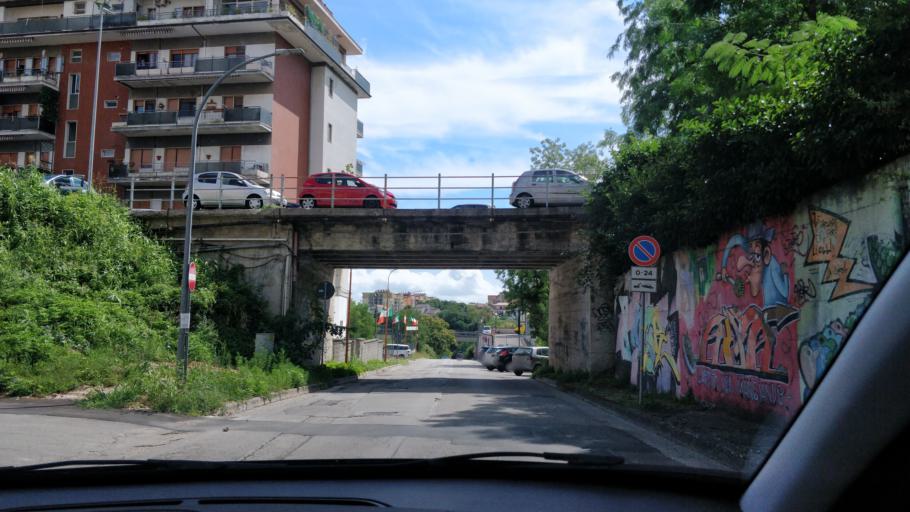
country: IT
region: Abruzzo
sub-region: Provincia di Chieti
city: Lanciano
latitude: 42.2291
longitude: 14.3988
